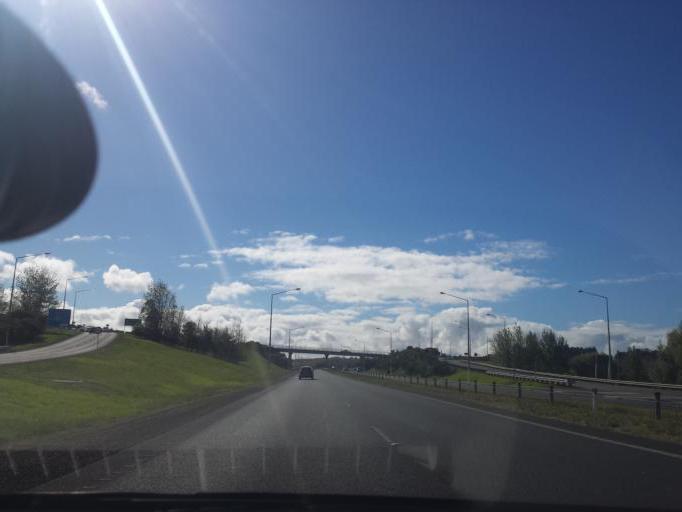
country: NZ
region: Auckland
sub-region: Auckland
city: Rothesay Bay
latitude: -36.6277
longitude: 174.6628
